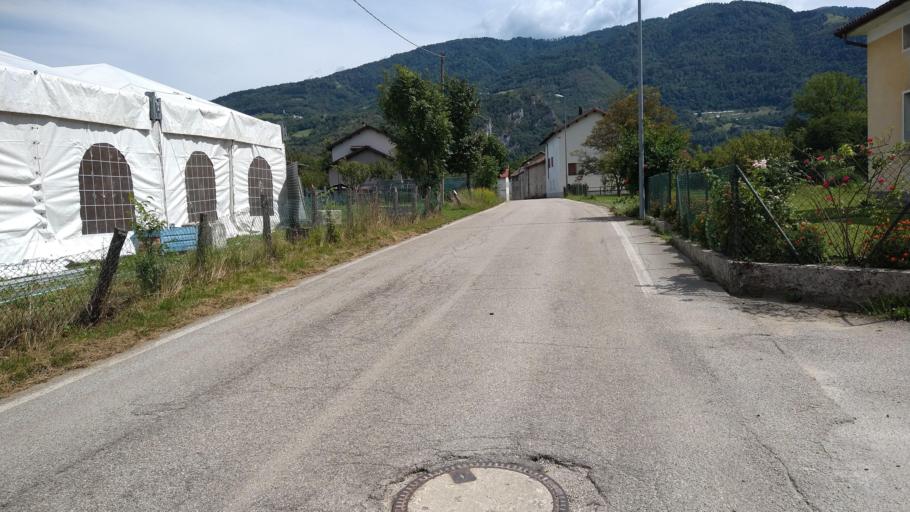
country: IT
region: Veneto
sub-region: Provincia di Belluno
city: Villabruna-Umin
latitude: 46.0110
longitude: 11.9642
